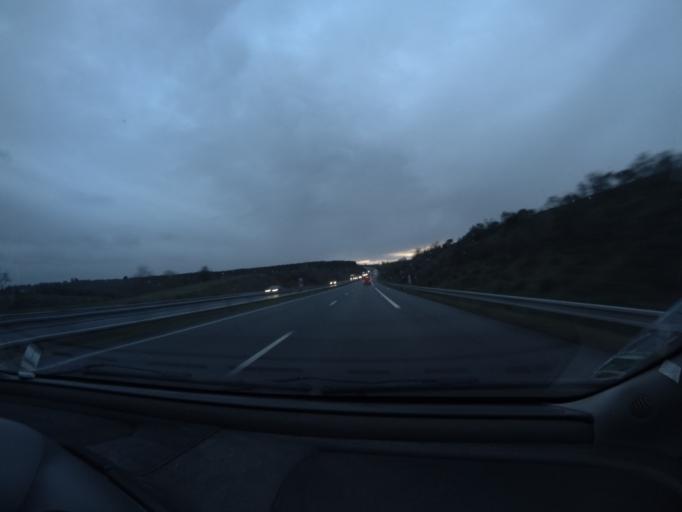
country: FR
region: Pays de la Loire
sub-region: Departement de Maine-et-Loire
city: Champtoce-sur-Loire
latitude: 47.4354
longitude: -0.8566
